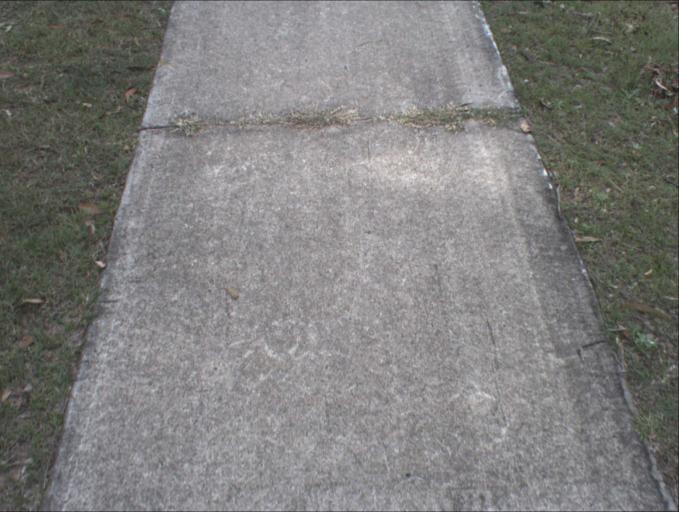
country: AU
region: Queensland
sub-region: Logan
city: Logan Reserve
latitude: -27.7218
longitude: 153.0905
